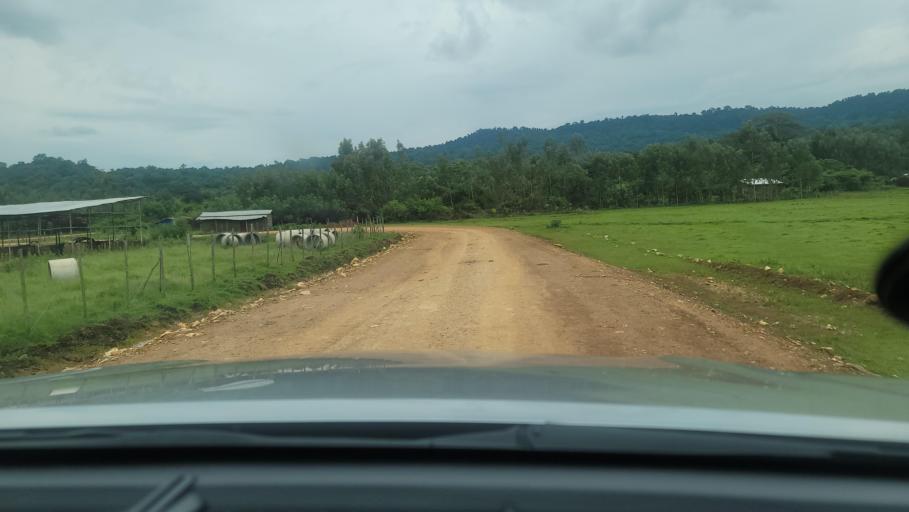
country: ET
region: Oromiya
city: Agaro
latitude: 7.7657
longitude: 36.3154
